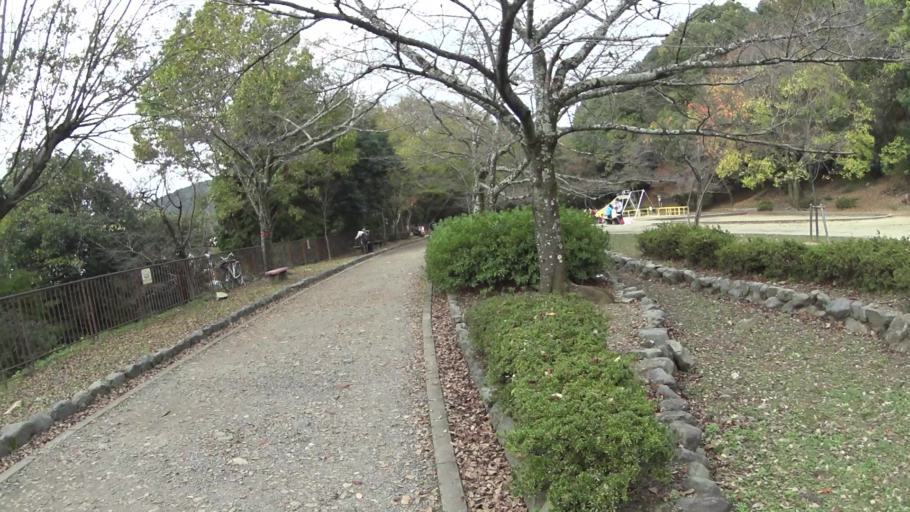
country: JP
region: Shiga Prefecture
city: Otsu-shi
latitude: 34.9933
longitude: 135.8222
